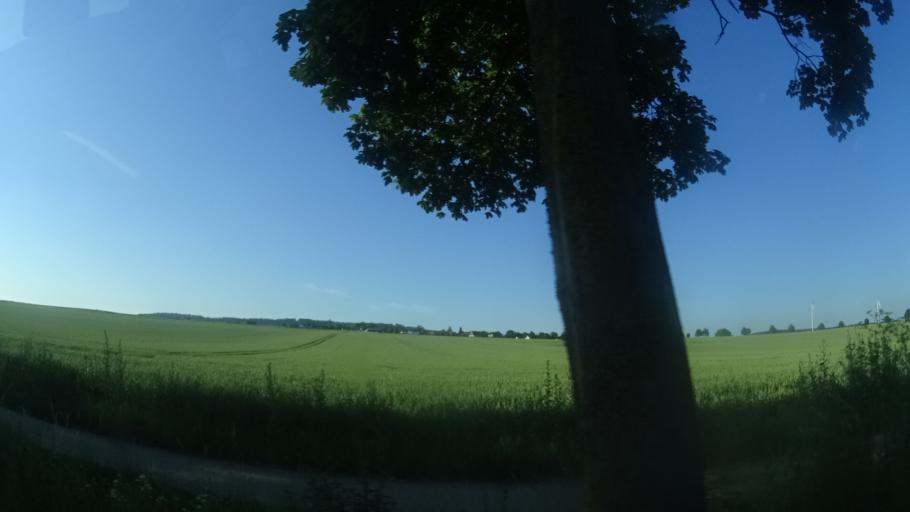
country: DE
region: Lower Saxony
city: Bad Salzdetfurth
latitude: 52.1065
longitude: 10.0242
